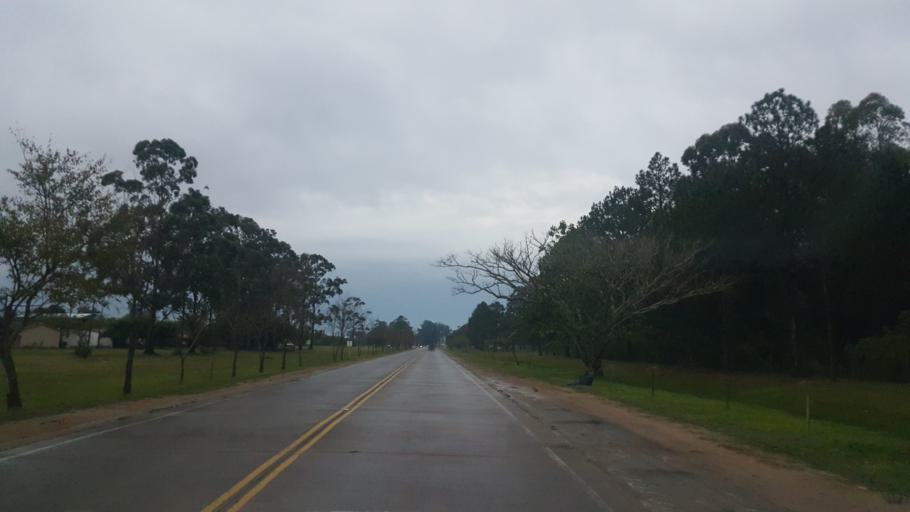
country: AR
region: Corrientes
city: Ituzaingo
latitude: -27.5866
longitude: -56.6811
